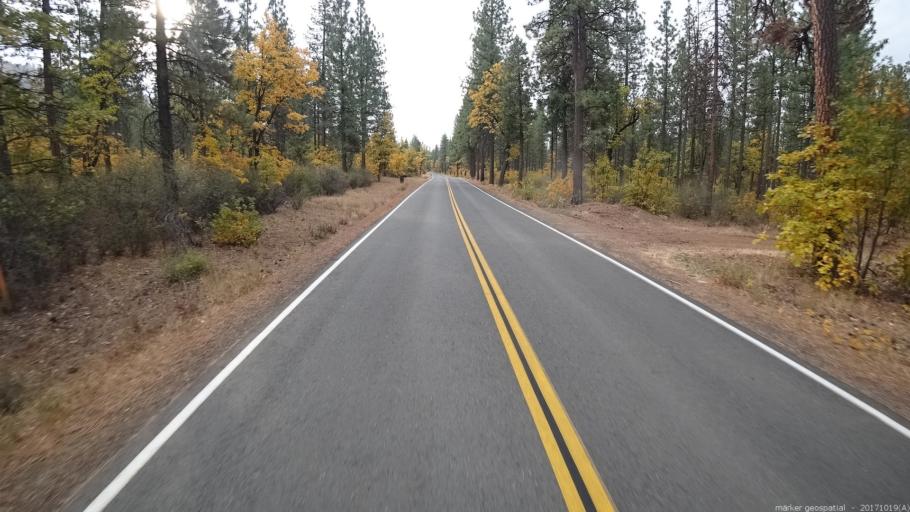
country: US
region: California
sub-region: Shasta County
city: Burney
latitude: 41.1727
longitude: -121.3612
